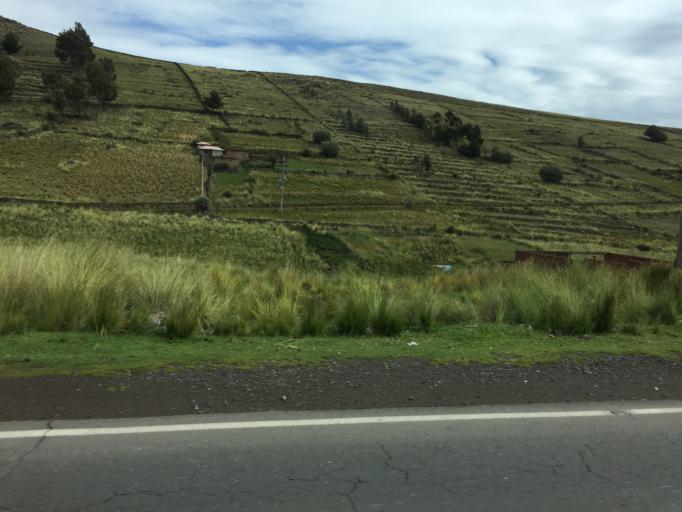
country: PE
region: Puno
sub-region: Provincia de Chucuito
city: Juli
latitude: -16.2073
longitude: -69.4348
